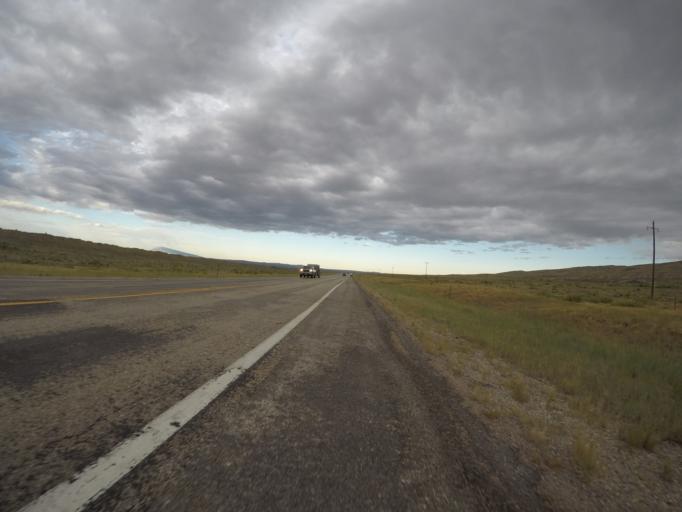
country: US
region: Wyoming
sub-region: Albany County
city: Laramie
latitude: 41.8650
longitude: -106.0911
